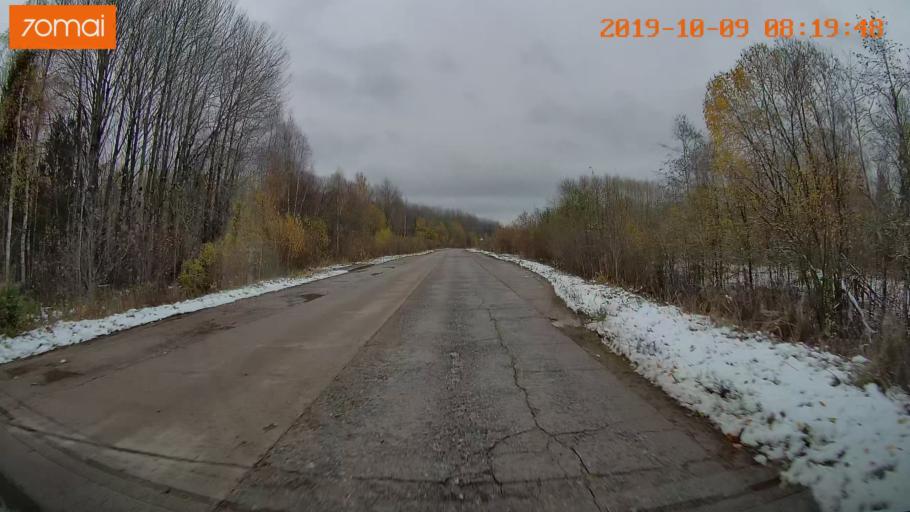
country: RU
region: Vologda
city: Gryazovets
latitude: 58.7426
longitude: 40.2486
